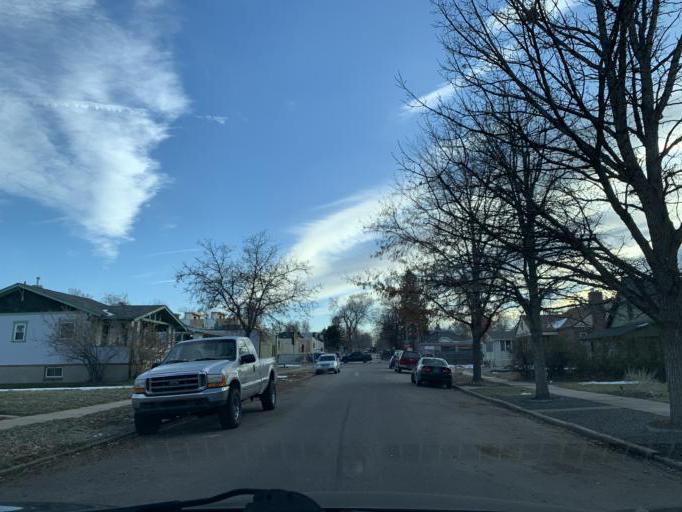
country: US
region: Colorado
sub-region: Jefferson County
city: Edgewater
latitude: 39.7774
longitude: -105.0521
